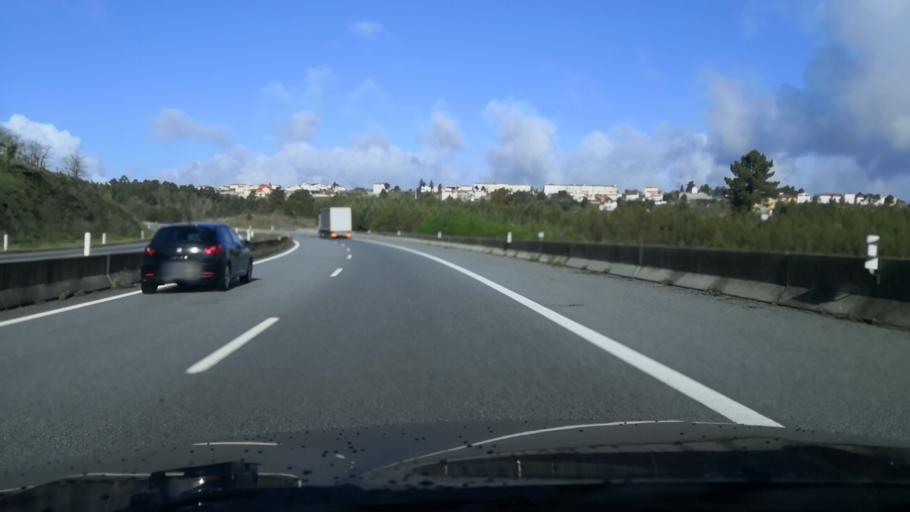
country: PT
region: Guarda
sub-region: Celorico da Beira
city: Celorico da Beira
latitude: 40.6278
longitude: -7.3840
